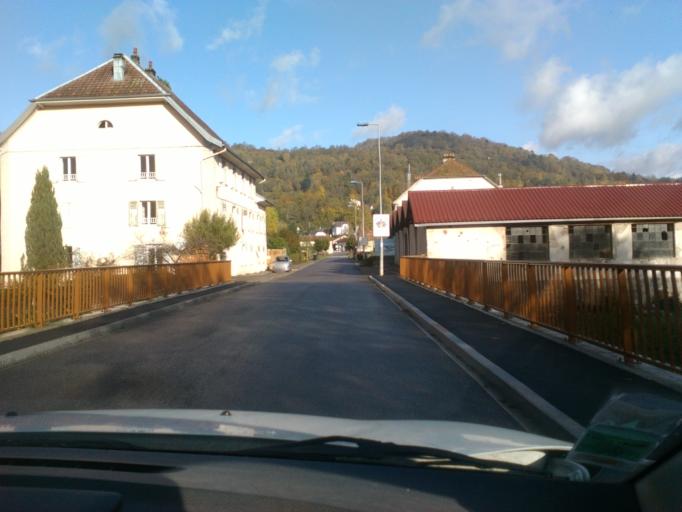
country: FR
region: Lorraine
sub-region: Departement des Vosges
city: Saulxures-sur-Moselotte
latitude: 47.9460
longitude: 6.7691
